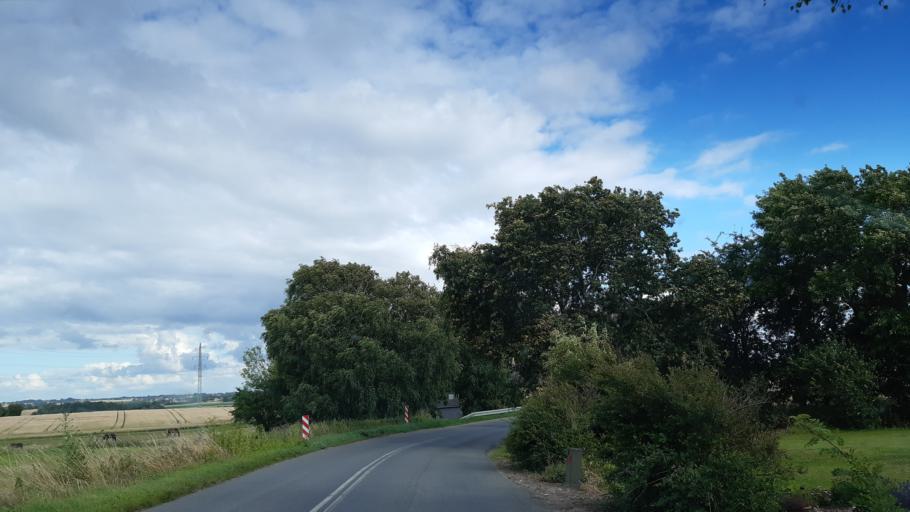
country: DK
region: Zealand
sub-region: Odsherred Kommune
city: Horve
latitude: 55.8125
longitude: 11.4309
